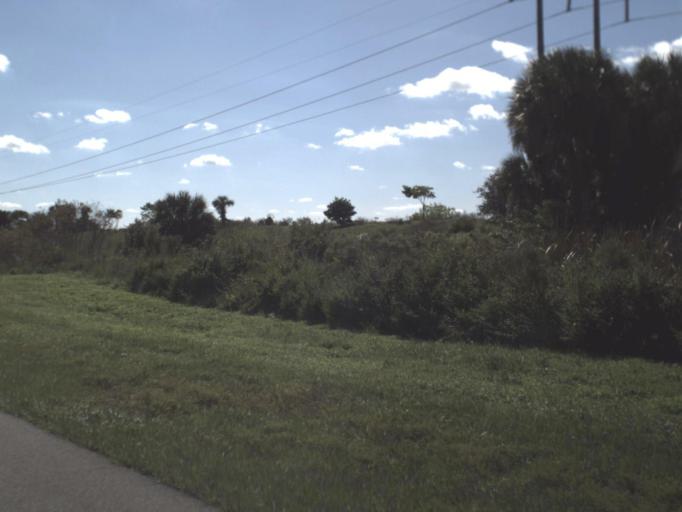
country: US
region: Florida
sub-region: Lee County
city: Lehigh Acres
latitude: 26.5283
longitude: -81.6028
